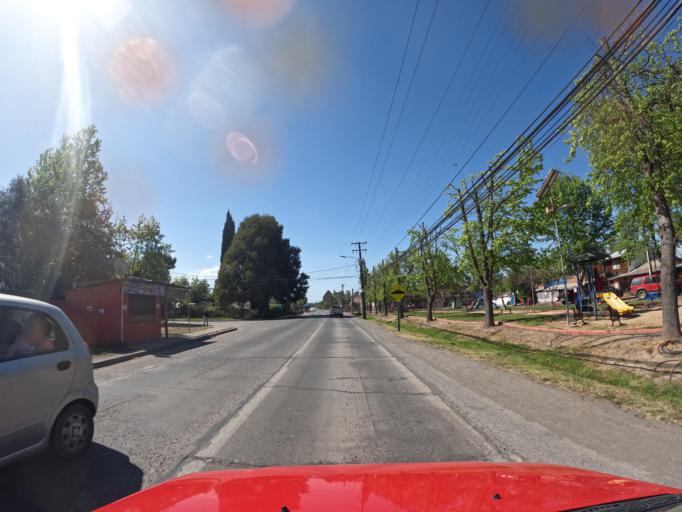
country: CL
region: Maule
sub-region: Provincia de Curico
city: Molina
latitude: -35.0733
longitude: -71.2566
